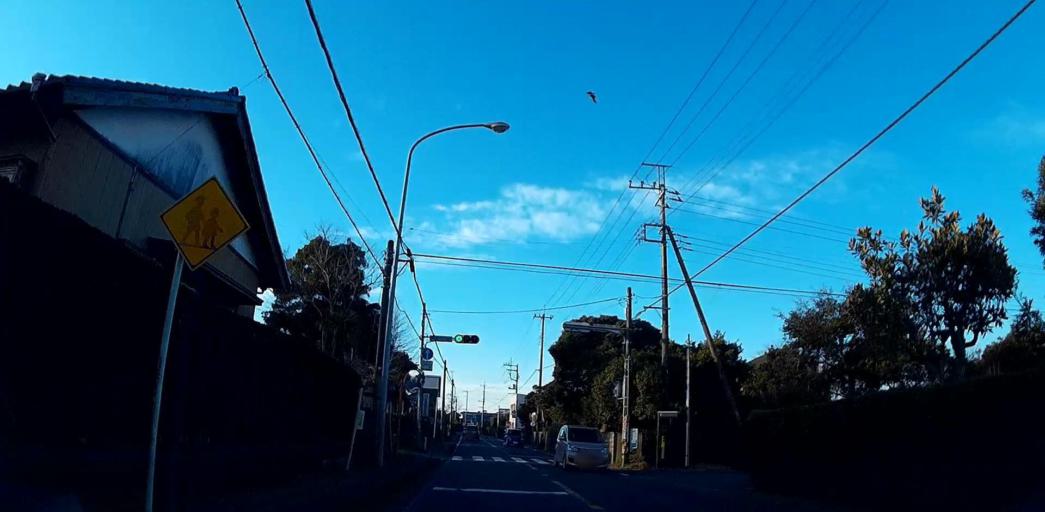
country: JP
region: Chiba
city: Omigawa
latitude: 35.8752
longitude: 140.5876
